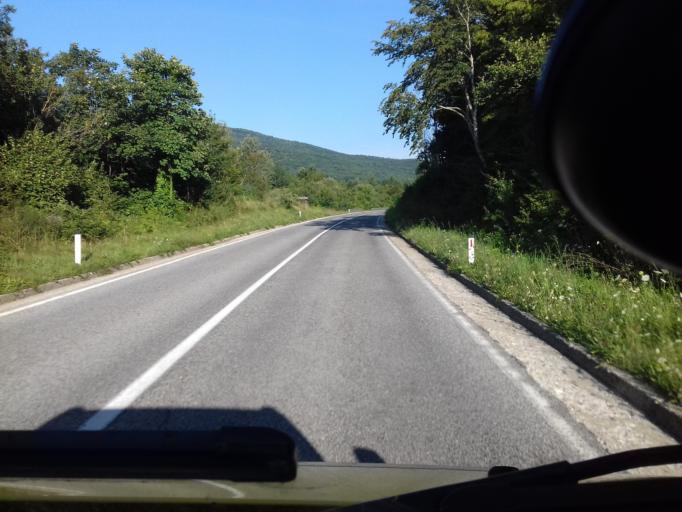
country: BA
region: Federation of Bosnia and Herzegovina
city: Orasac
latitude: 44.6618
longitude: 16.1471
